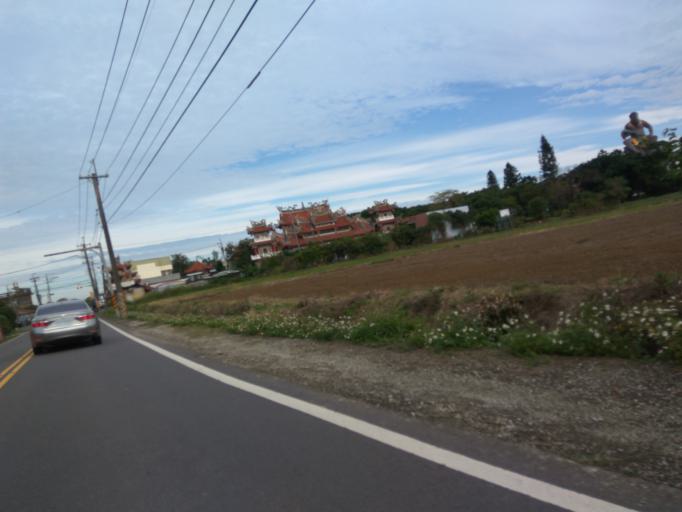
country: TW
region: Taiwan
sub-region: Hsinchu
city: Zhubei
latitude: 24.9591
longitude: 121.1182
